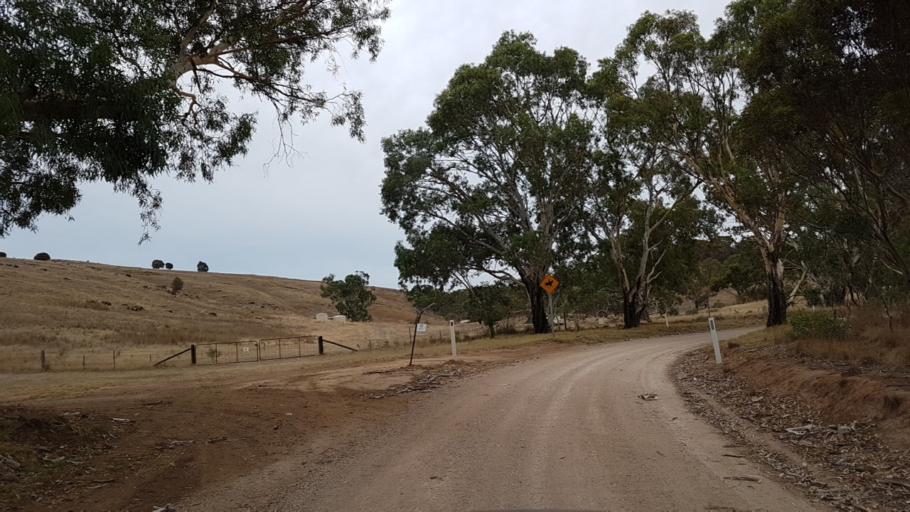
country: AU
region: South Australia
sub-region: Mount Barker
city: Callington
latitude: -35.0067
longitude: 139.0324
